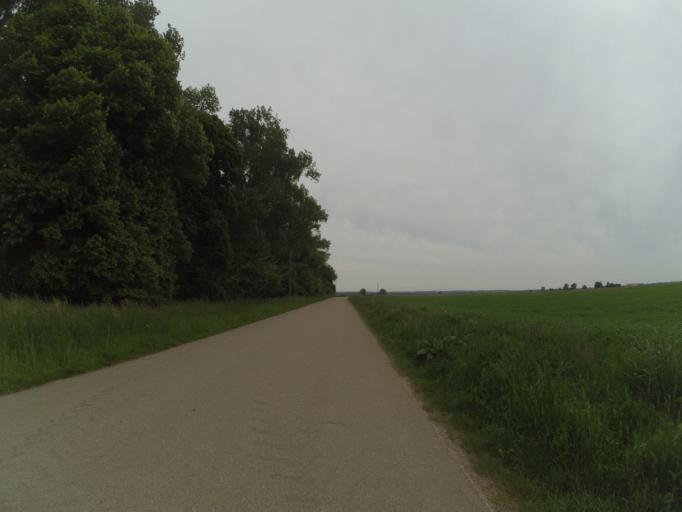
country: DE
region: Baden-Wuerttemberg
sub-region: Regierungsbezirk Stuttgart
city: Sontheim an der Brenz
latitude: 48.5300
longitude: 10.2868
